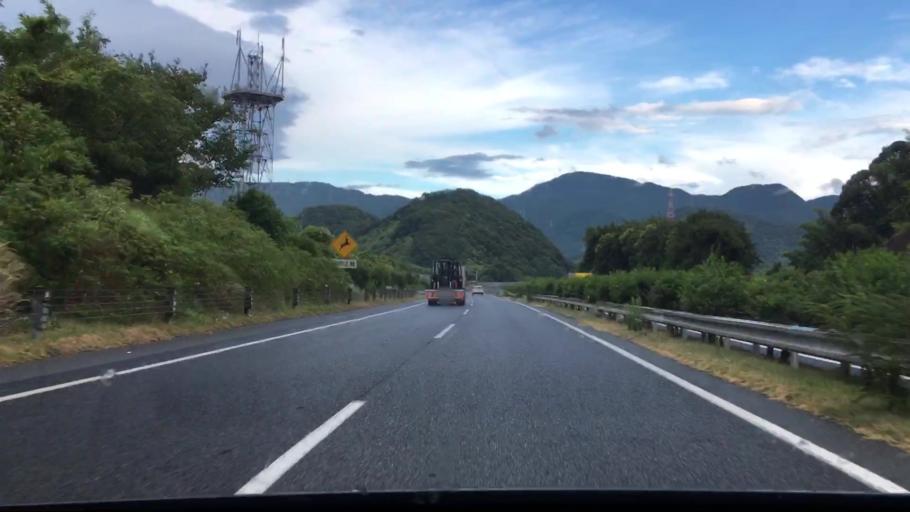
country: JP
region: Fukuoka
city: Kitakyushu
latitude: 33.8021
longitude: 130.8573
